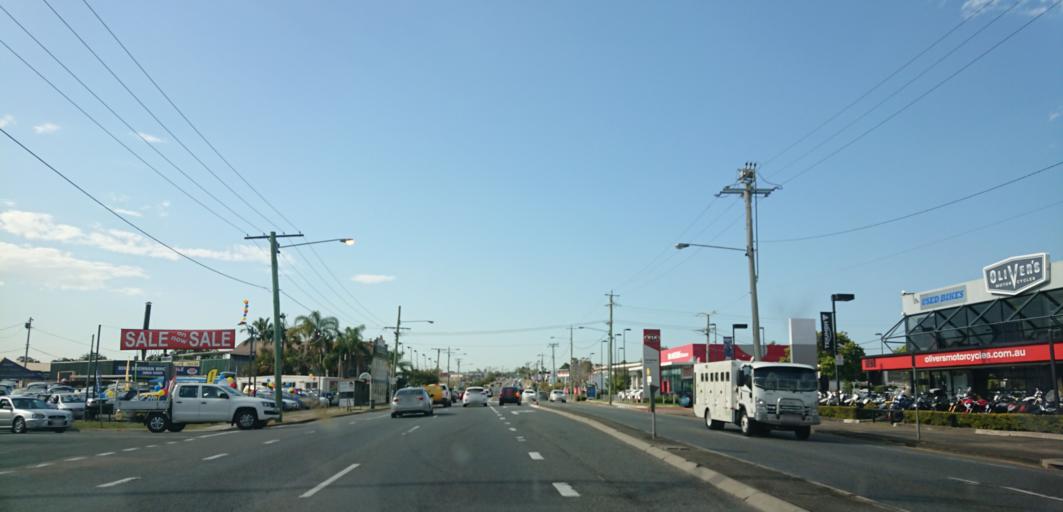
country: AU
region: Queensland
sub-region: Brisbane
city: Rocklea
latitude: -27.5350
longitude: 153.0148
